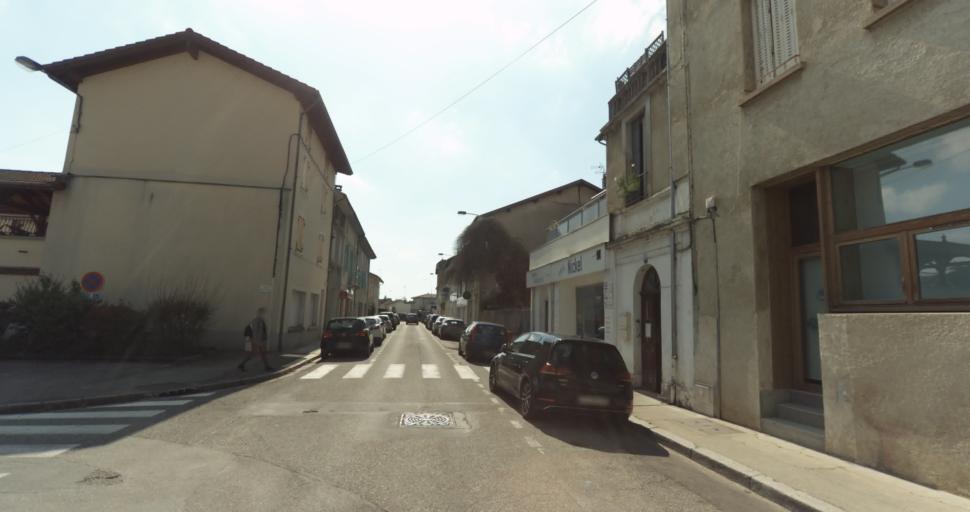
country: FR
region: Rhone-Alpes
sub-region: Departement de l'Isere
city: Saint-Marcellin
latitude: 45.1520
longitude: 5.3186
